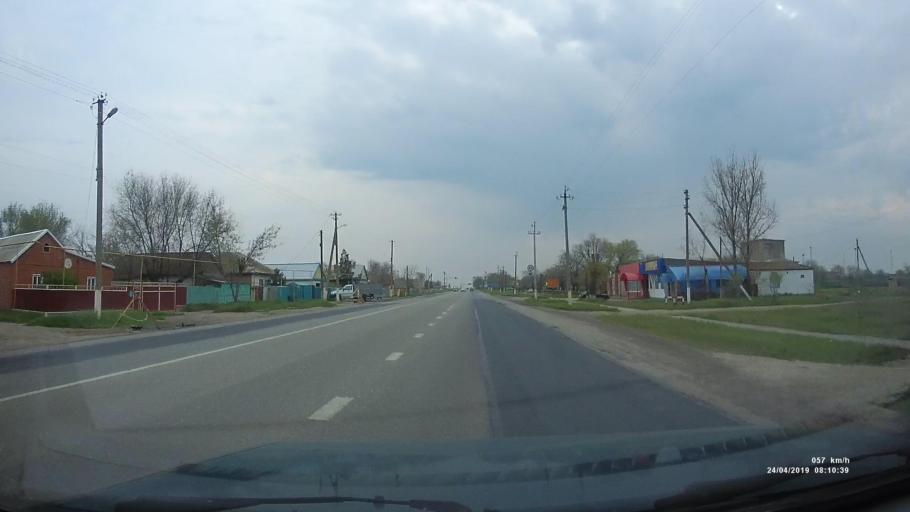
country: RU
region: Kalmykiya
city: Priyutnoye
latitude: 46.0996
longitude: 43.5190
